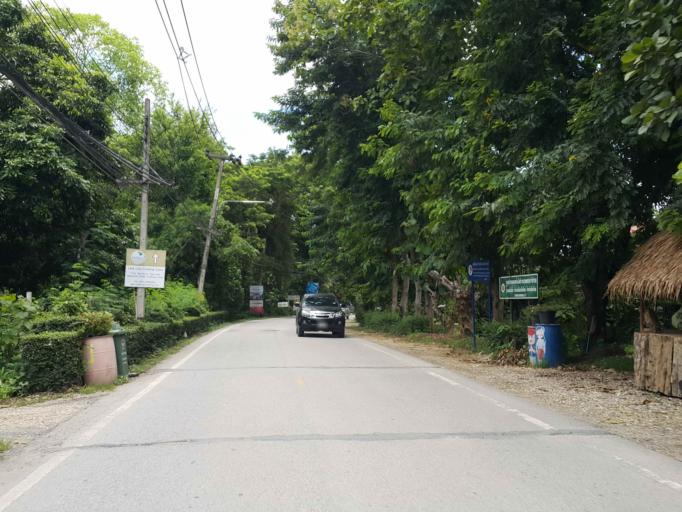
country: TH
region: Chiang Mai
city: San Sai
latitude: 18.8513
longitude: 98.9867
